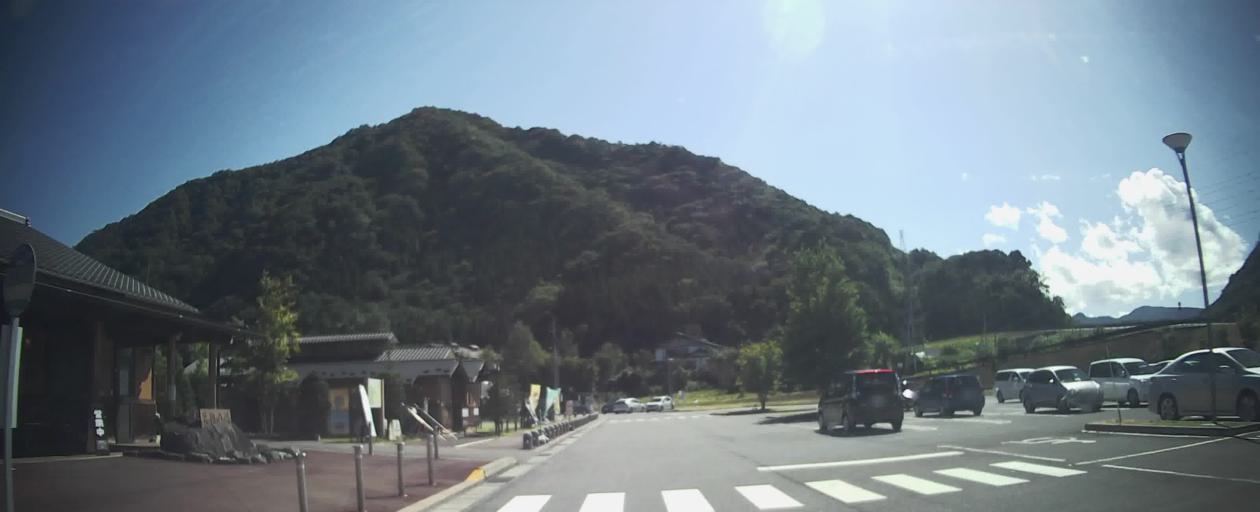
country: JP
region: Gunma
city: Nakanojomachi
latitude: 36.5702
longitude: 138.7354
